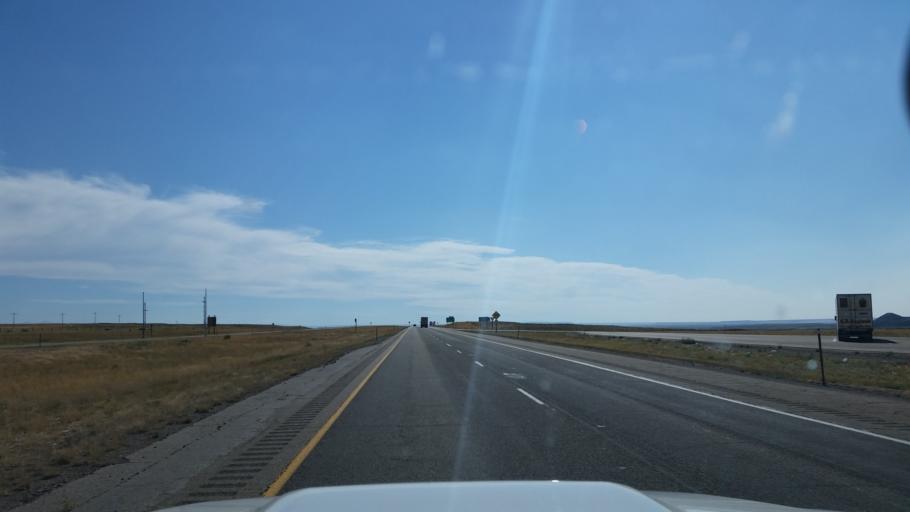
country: US
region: Wyoming
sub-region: Uinta County
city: Lyman
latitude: 41.3982
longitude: -110.1737
